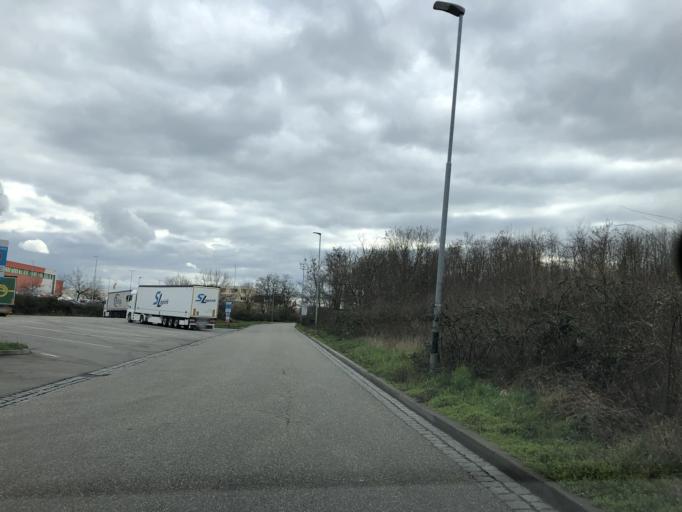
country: DE
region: Baden-Wuerttemberg
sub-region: Karlsruhe Region
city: Walldorf
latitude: 49.2994
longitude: 8.6698
